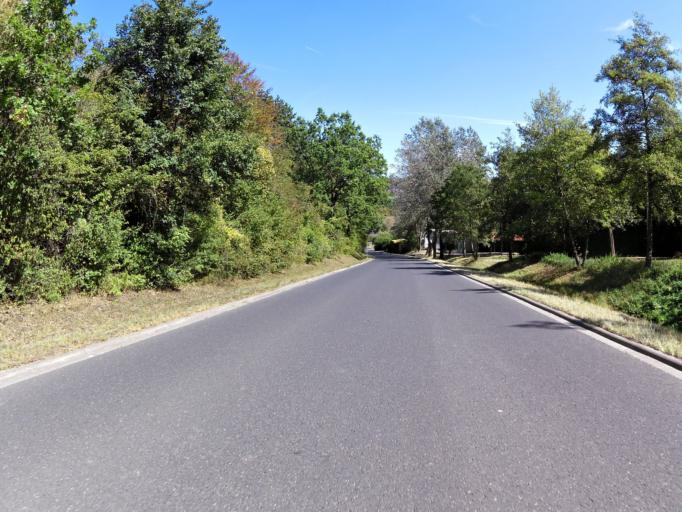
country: DE
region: Bavaria
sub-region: Regierungsbezirk Unterfranken
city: Guntersleben
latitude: 49.8602
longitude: 9.8997
